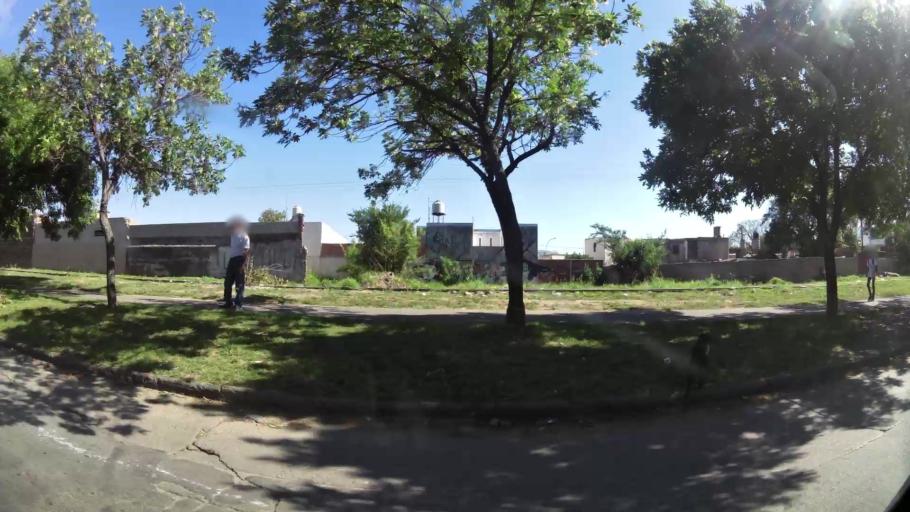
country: AR
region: Cordoba
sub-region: Departamento de Capital
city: Cordoba
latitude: -31.4405
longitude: -64.1618
